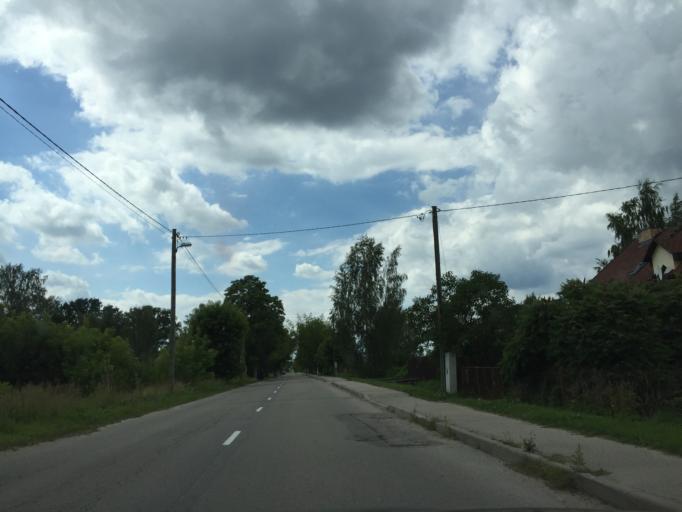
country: LV
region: Jelgava
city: Jelgava
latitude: 56.6254
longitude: 23.7132
